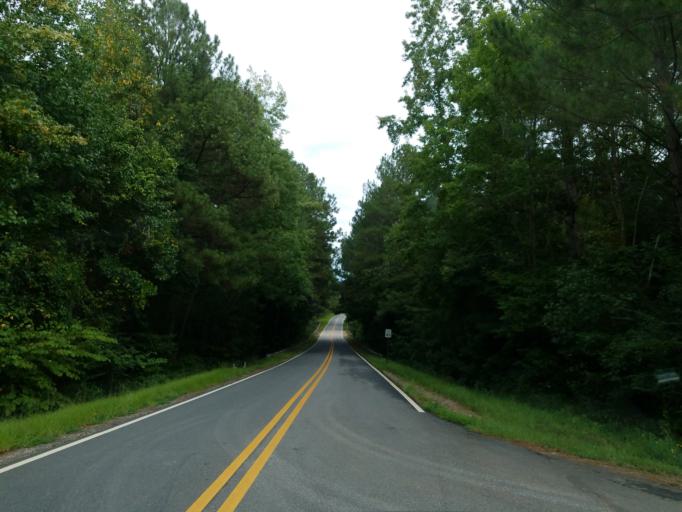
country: US
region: Georgia
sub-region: Bibb County
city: West Point
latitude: 32.9053
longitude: -83.8804
